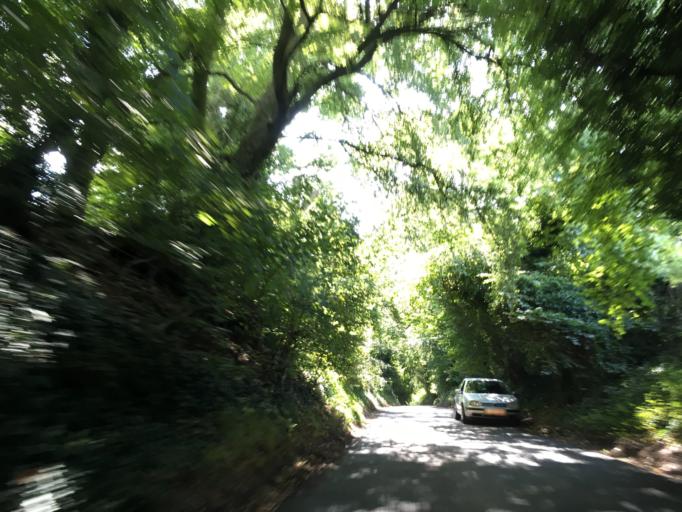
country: GB
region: England
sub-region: Hampshire
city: Colden Common
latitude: 51.0221
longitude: -1.2722
